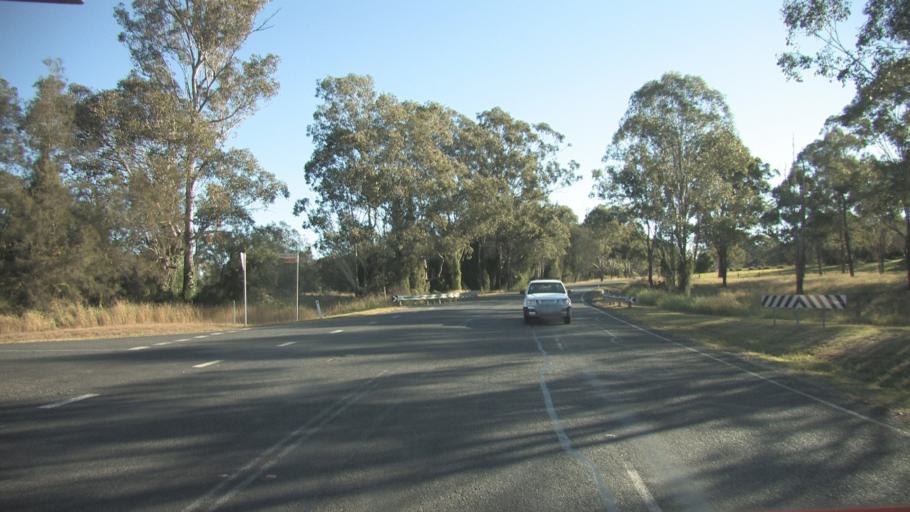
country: AU
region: Queensland
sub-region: Logan
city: North Maclean
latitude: -27.7596
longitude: 153.0456
